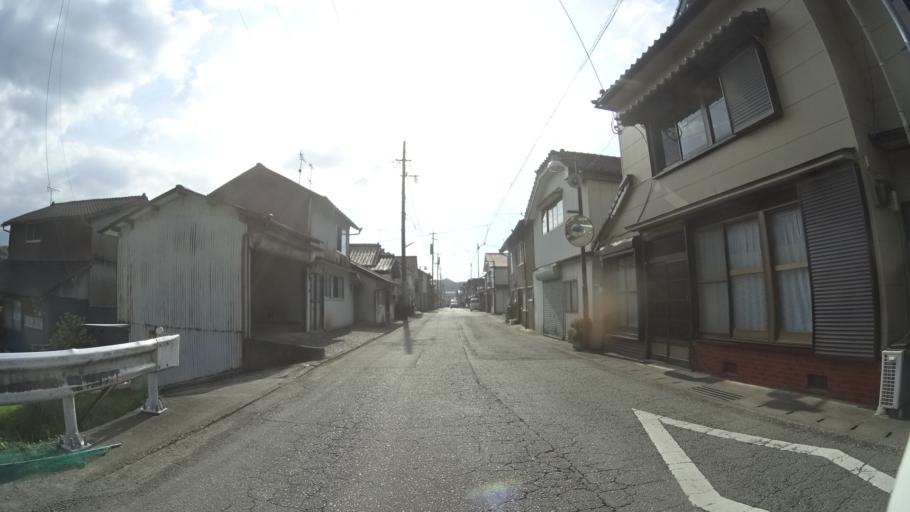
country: JP
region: Kumamoto
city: Ozu
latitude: 32.6865
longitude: 130.9964
